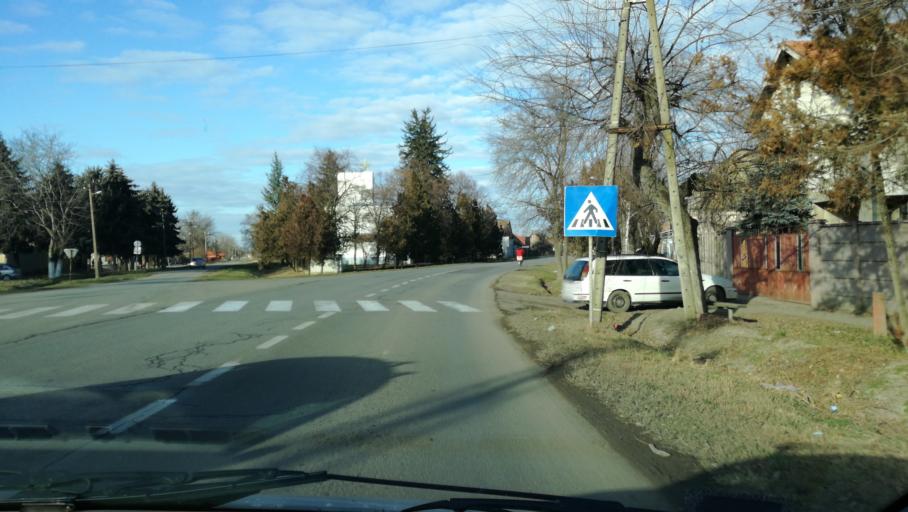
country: RS
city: Ostojicevo
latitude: 45.8905
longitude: 20.1648
